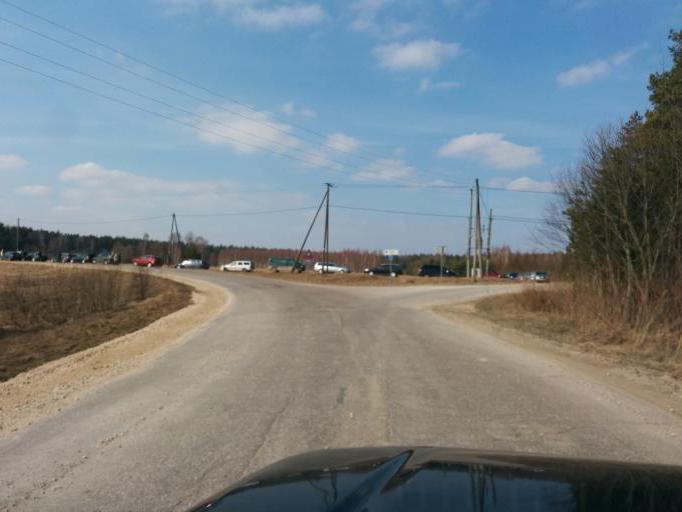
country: LV
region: Kekava
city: Kekava
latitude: 56.8499
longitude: 24.2406
